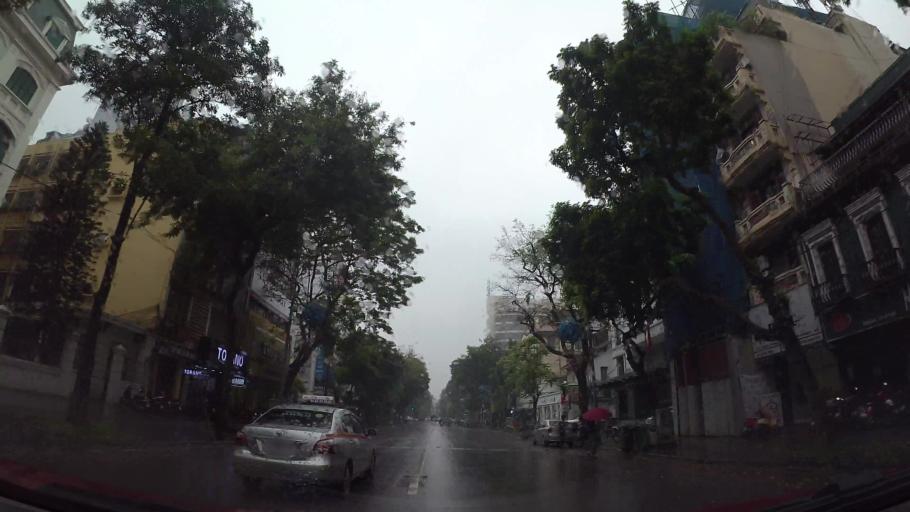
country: VN
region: Ha Noi
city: Hoan Kiem
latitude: 21.0244
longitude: 105.8511
